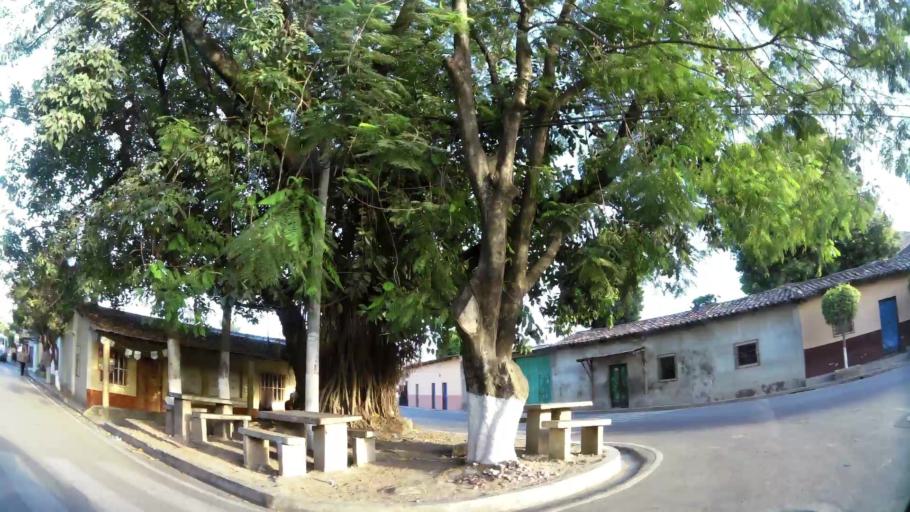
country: SV
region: Santa Ana
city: Metapan
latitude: 14.3302
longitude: -89.4501
